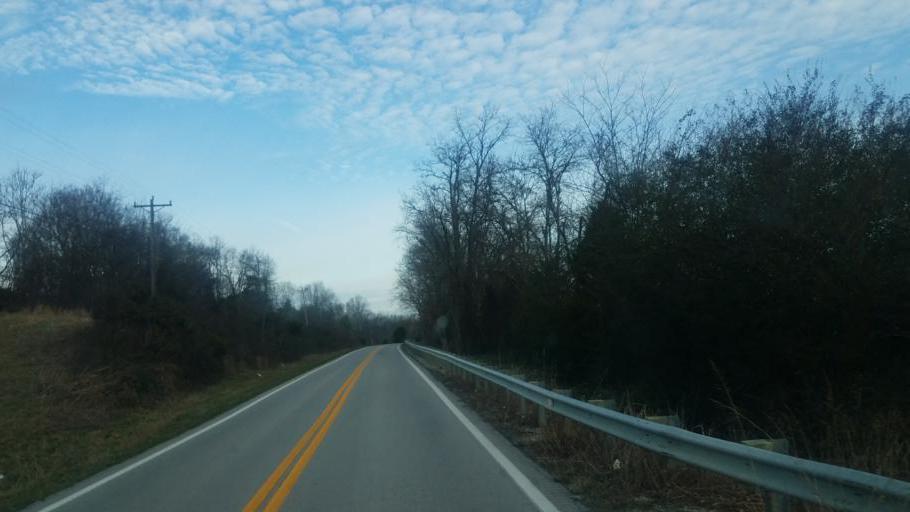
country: US
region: Kentucky
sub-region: Clinton County
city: Albany
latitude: 36.7909
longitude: -85.1799
